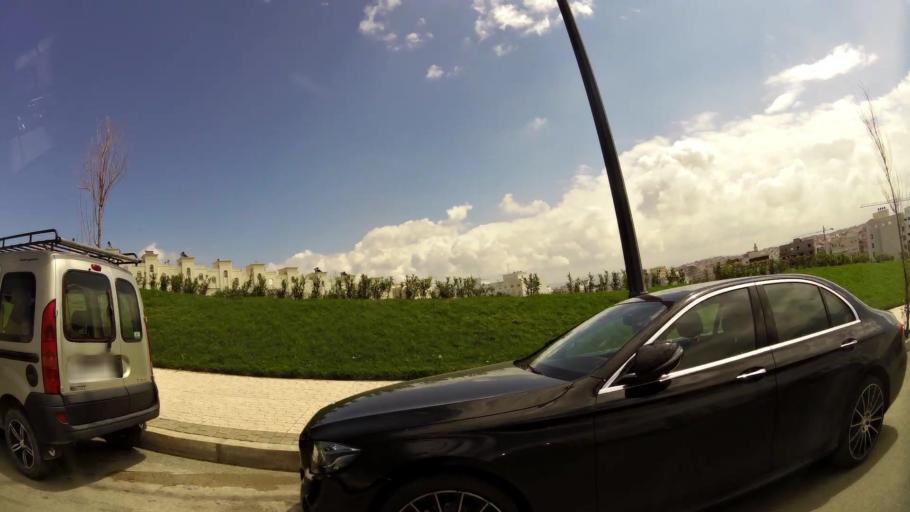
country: MA
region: Tanger-Tetouan
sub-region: Tanger-Assilah
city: Tangier
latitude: 35.7672
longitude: -5.8394
